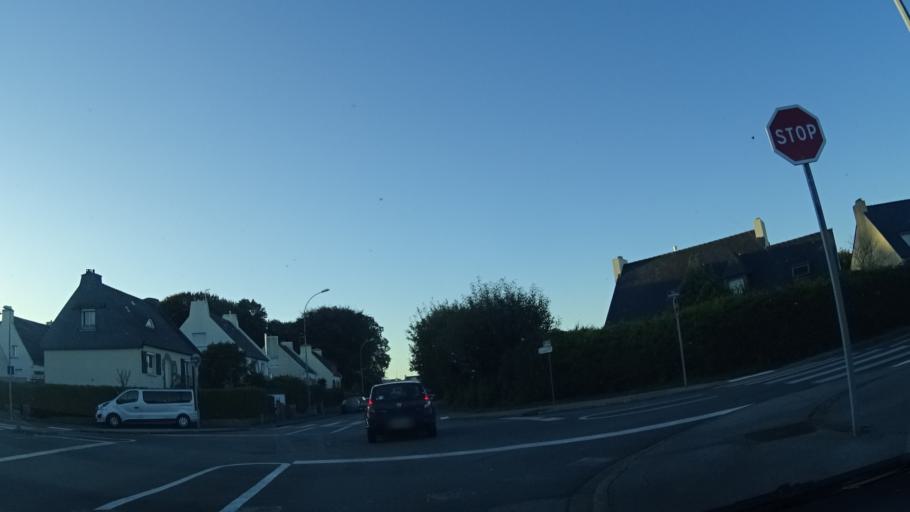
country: FR
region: Brittany
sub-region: Departement du Finistere
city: Guilers
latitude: 48.4235
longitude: -4.5628
